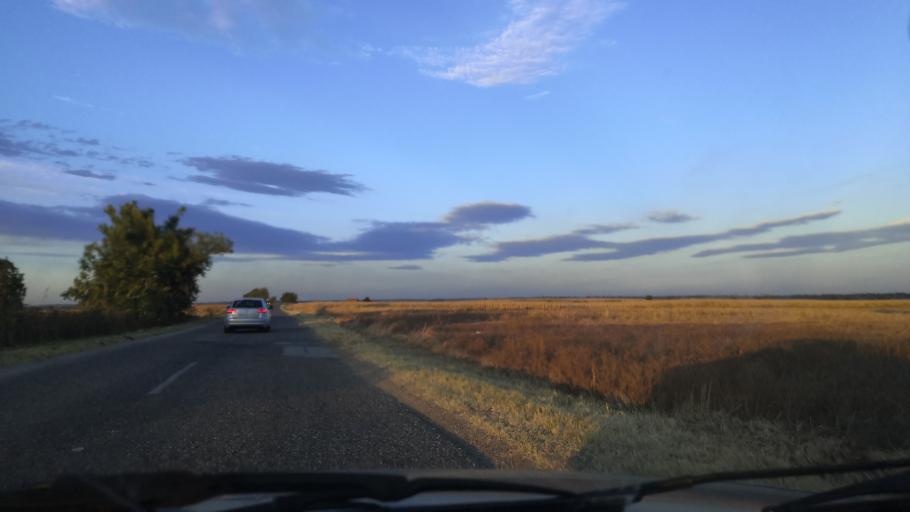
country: RO
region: Mehedinti
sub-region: Comuna Gruia
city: Izvoarele
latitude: 44.2549
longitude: 22.6290
